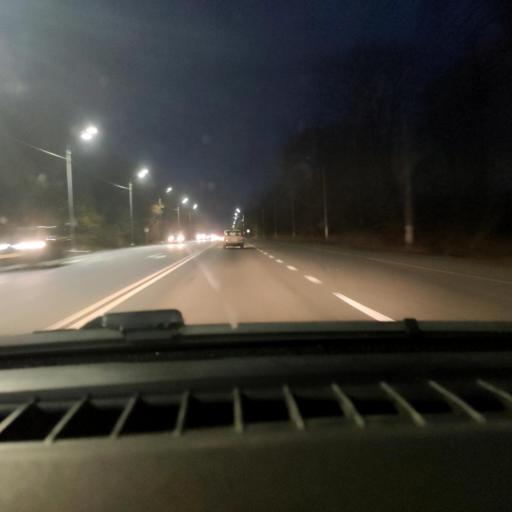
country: RU
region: Voronezj
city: Semiluki
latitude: 51.6397
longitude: 39.0106
